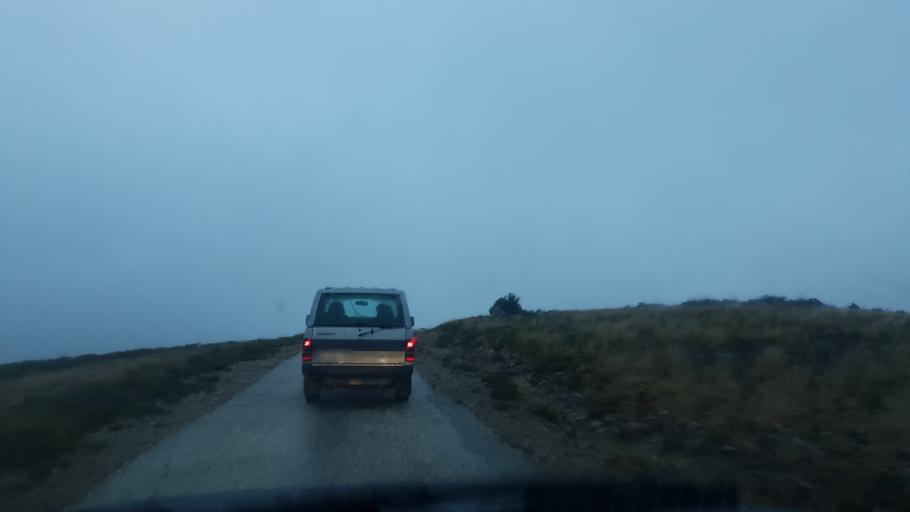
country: PT
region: Viseu
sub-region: Sao Pedro do Sul
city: Sao Pedro do Sul
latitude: 40.8298
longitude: -8.1252
